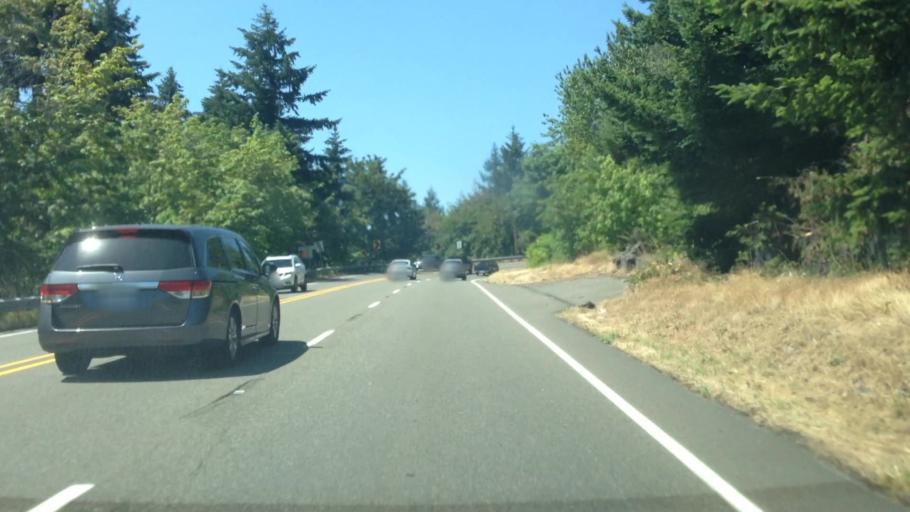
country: US
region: Washington
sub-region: Pierce County
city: North Puyallup
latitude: 47.2165
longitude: -122.2970
